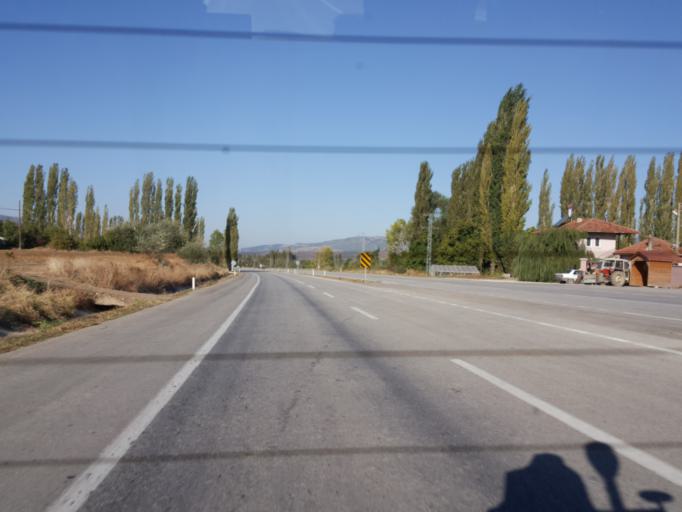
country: TR
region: Amasya
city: Ezinepazari
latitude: 40.5721
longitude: 36.1200
